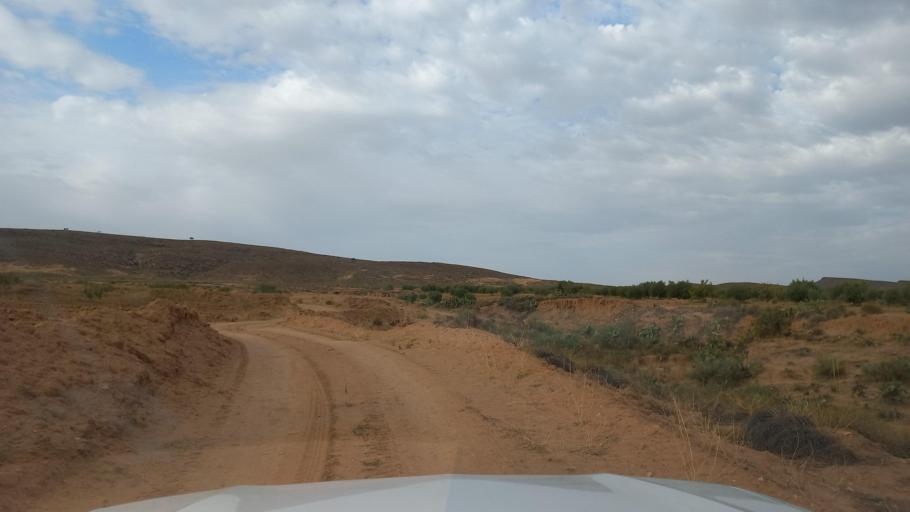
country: TN
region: Al Qasrayn
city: Kasserine
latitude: 35.1864
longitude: 9.0474
